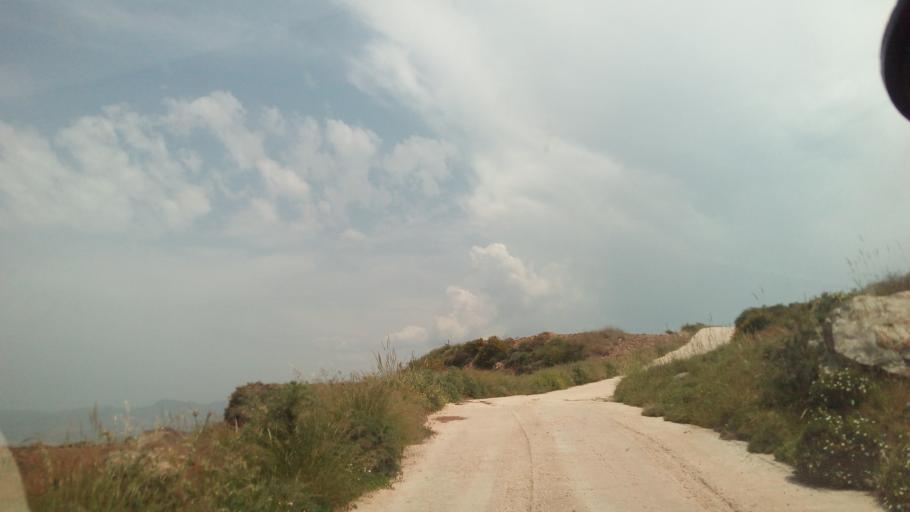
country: CY
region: Pafos
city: Polis
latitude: 34.9825
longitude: 32.3535
